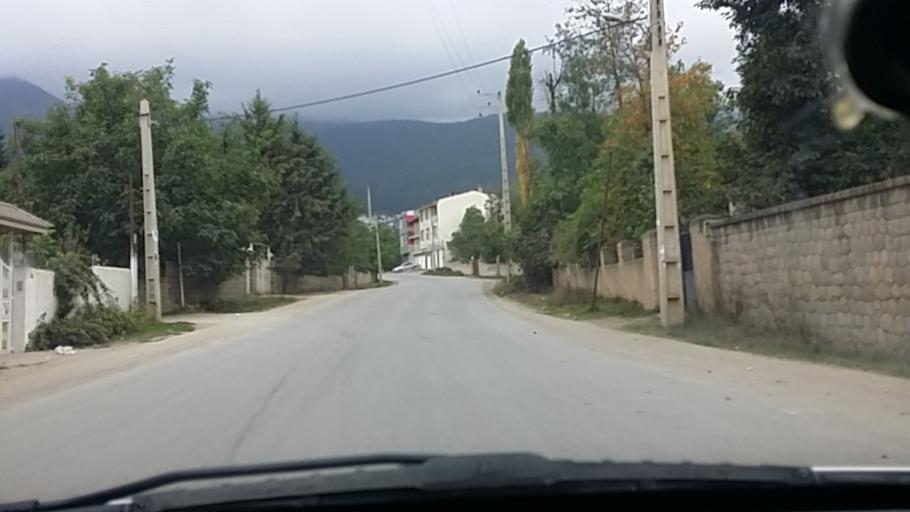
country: IR
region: Mazandaran
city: `Abbasabad
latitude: 36.5034
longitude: 51.1635
